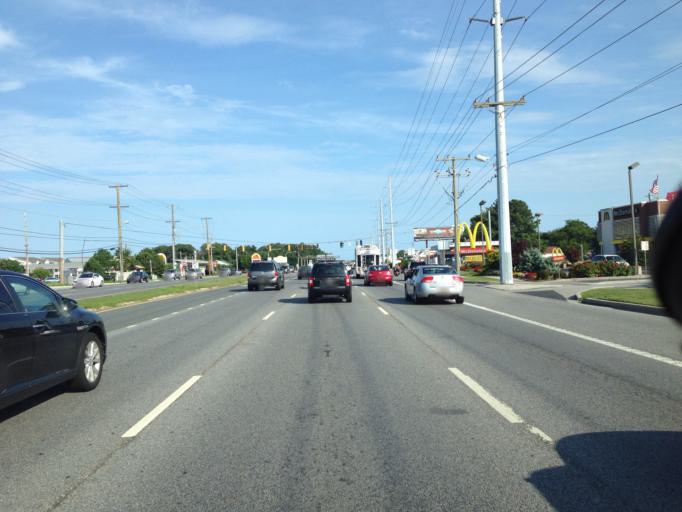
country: US
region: Delaware
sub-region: Sussex County
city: Lewes
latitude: 38.7325
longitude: -75.1350
